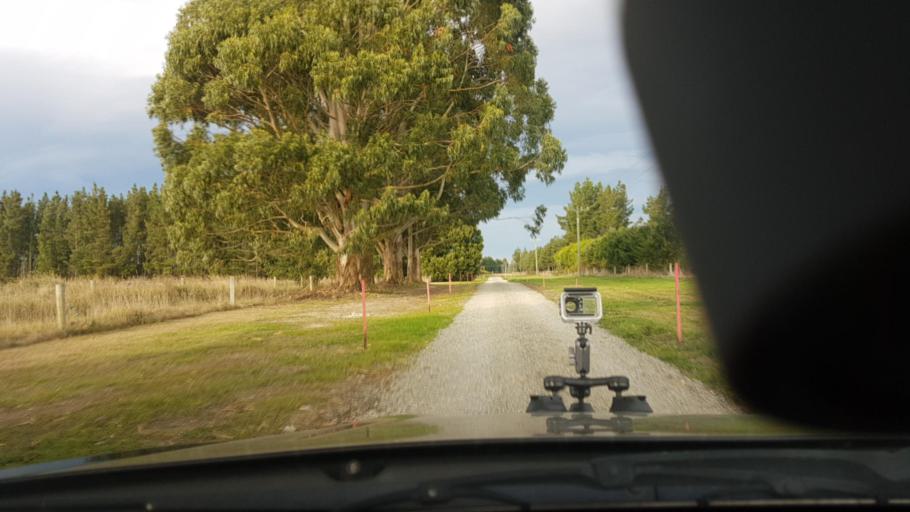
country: NZ
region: Canterbury
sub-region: Waimakariri District
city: Oxford
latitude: -43.3944
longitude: 172.2984
